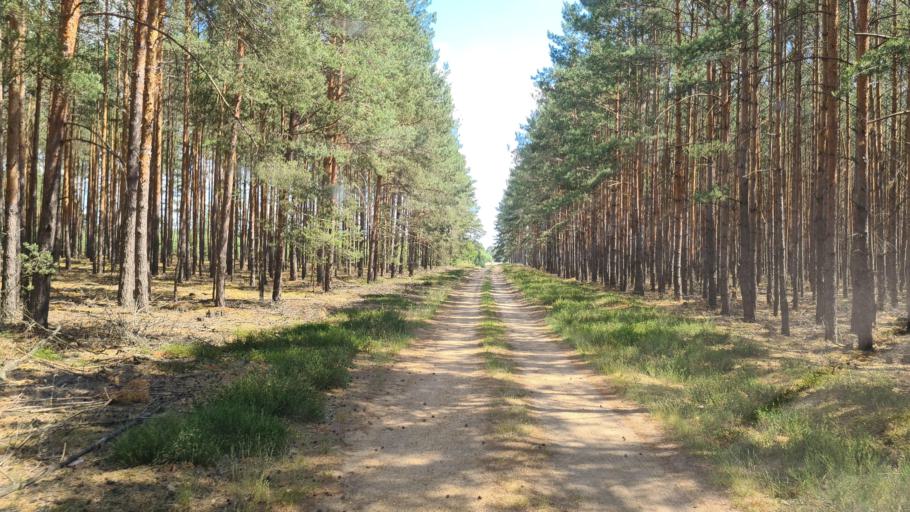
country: DE
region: Brandenburg
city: Sallgast
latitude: 51.6563
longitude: 13.8083
